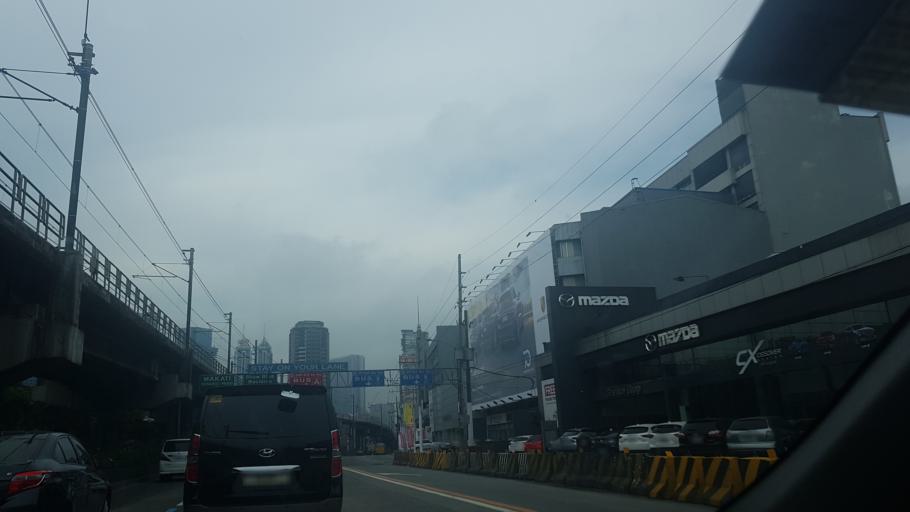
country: PH
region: Metro Manila
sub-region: Pasig
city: Pasig City
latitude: 14.5980
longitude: 121.0591
